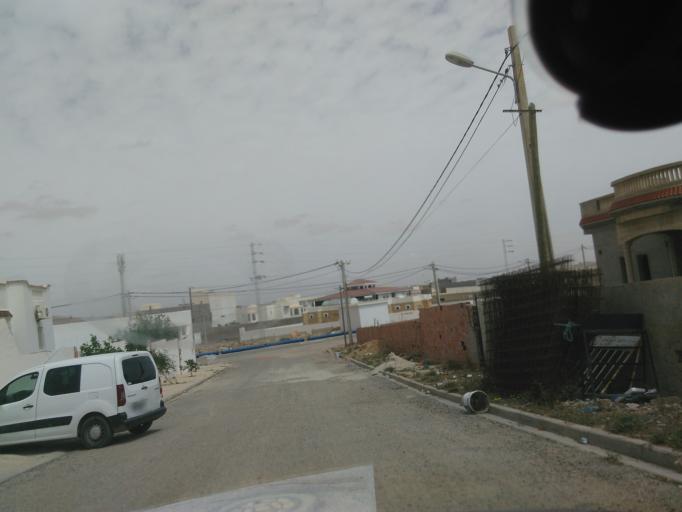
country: TN
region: Tataouine
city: Tataouine
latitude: 32.9449
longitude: 10.4666
